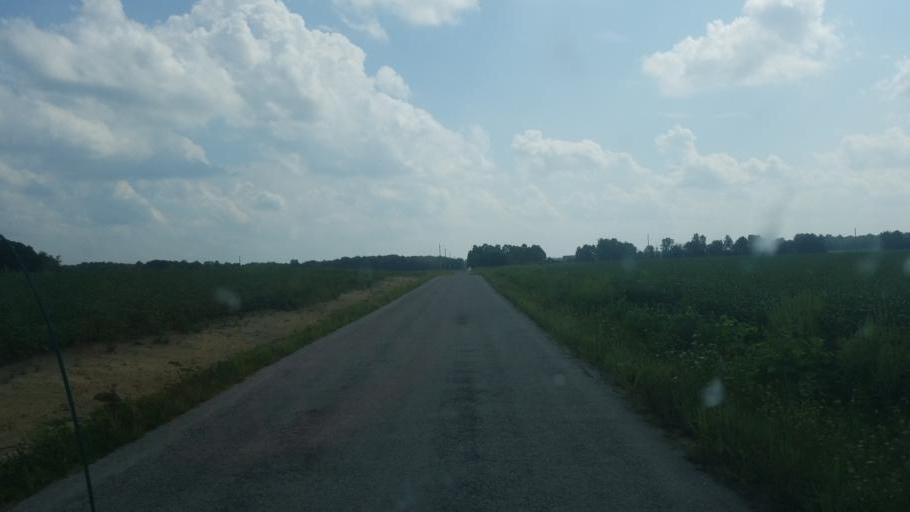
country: US
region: Ohio
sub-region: Huron County
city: New London
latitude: 41.0520
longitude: -82.3753
